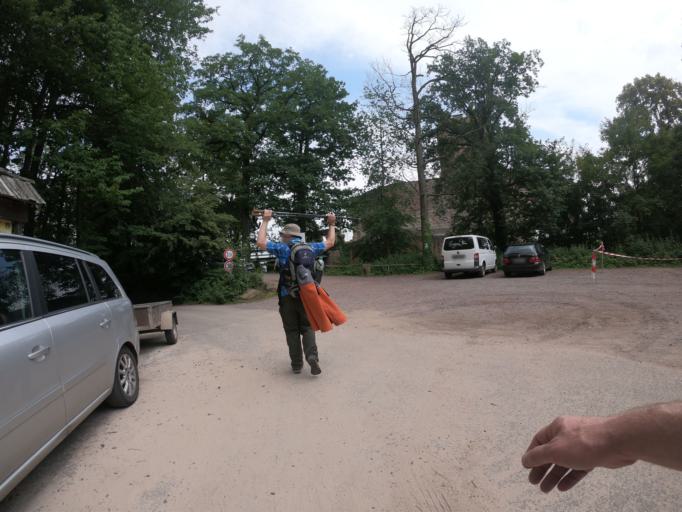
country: DE
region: Rheinland-Pfalz
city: Klingenmunster
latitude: 49.1415
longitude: 8.0055
